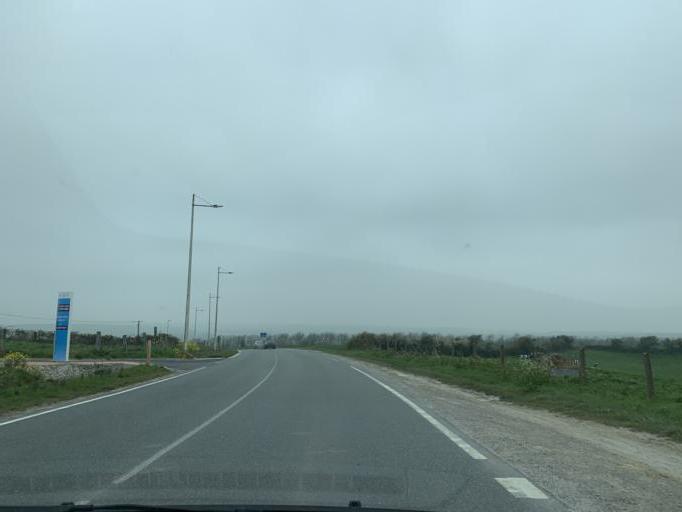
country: FR
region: Nord-Pas-de-Calais
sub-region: Departement du Pas-de-Calais
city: Marquise
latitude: 50.8265
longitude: 1.7050
